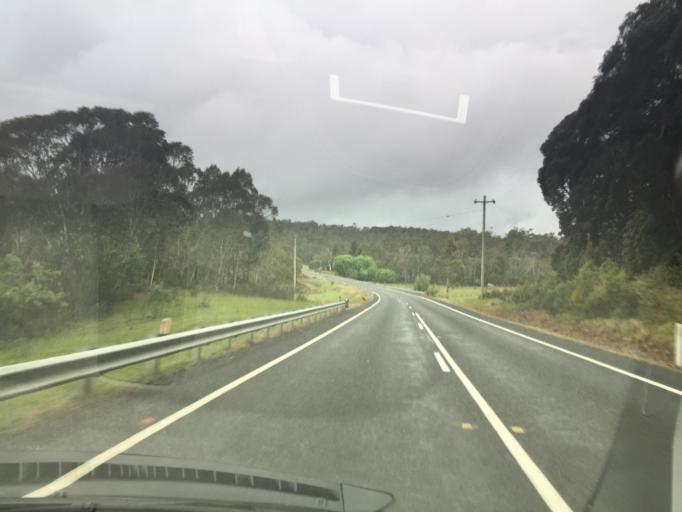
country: AU
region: New South Wales
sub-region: Bombala
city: Bombala
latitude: -36.6072
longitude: 149.3562
